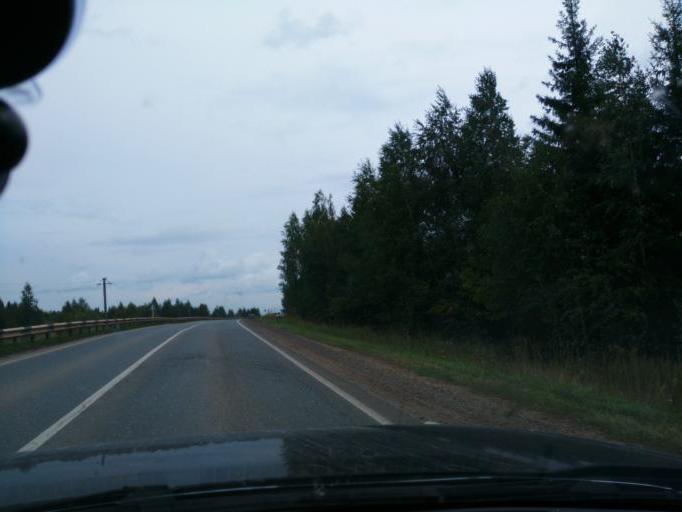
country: RU
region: Perm
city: Chernushka
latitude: 56.5091
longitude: 55.8833
